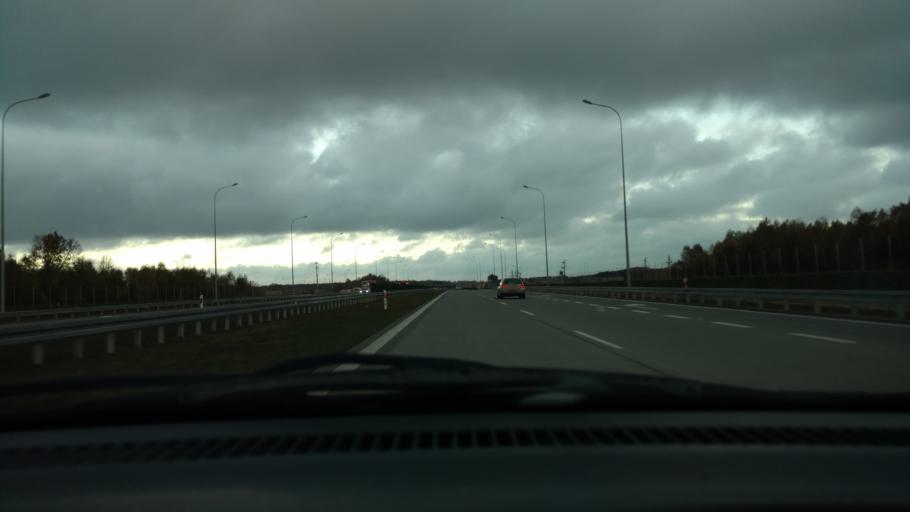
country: PL
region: Lodz Voivodeship
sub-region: Powiat lodzki wschodni
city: Andrespol
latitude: 51.6988
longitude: 19.6019
